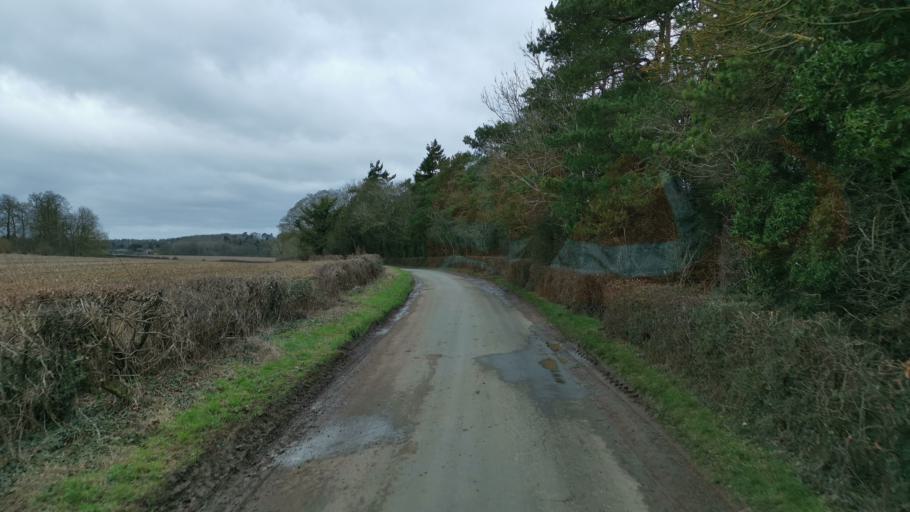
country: GB
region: England
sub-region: Oxfordshire
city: Somerton
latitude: 51.9000
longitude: -1.3093
